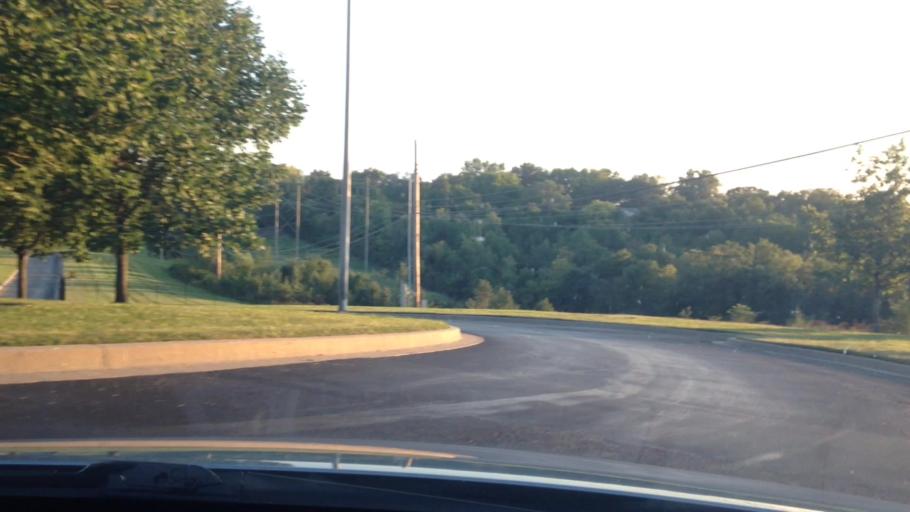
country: US
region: Missouri
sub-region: Jackson County
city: Grandview
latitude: 38.9246
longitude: -94.5594
